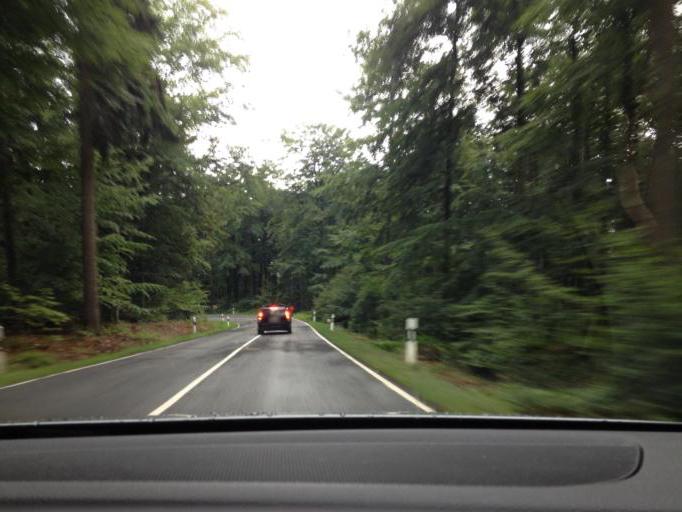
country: DE
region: Hesse
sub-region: Regierungsbezirk Darmstadt
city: Schlangenbad
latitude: 50.1011
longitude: 8.1446
